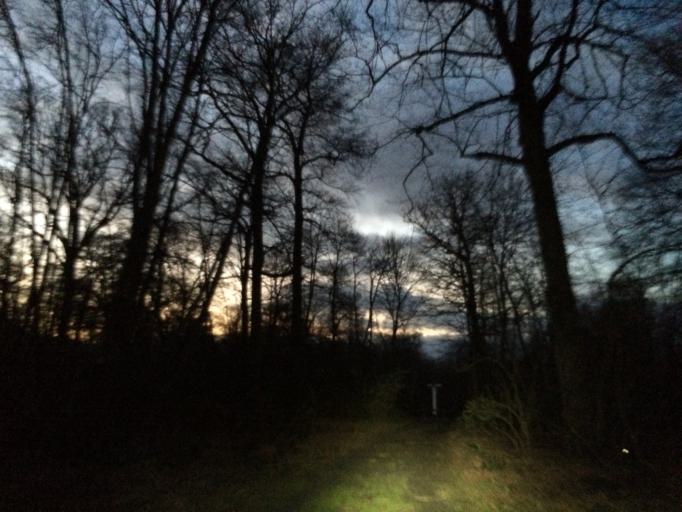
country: FR
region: Picardie
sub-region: Departement de l'Oise
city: Coye-la-Foret
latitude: 49.1530
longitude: 2.4804
